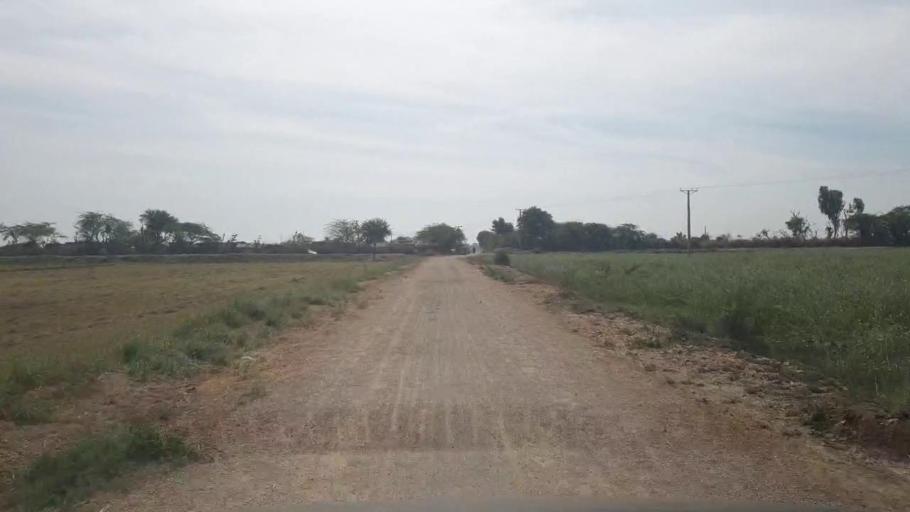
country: PK
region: Sindh
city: Umarkot
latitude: 25.3548
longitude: 69.6067
